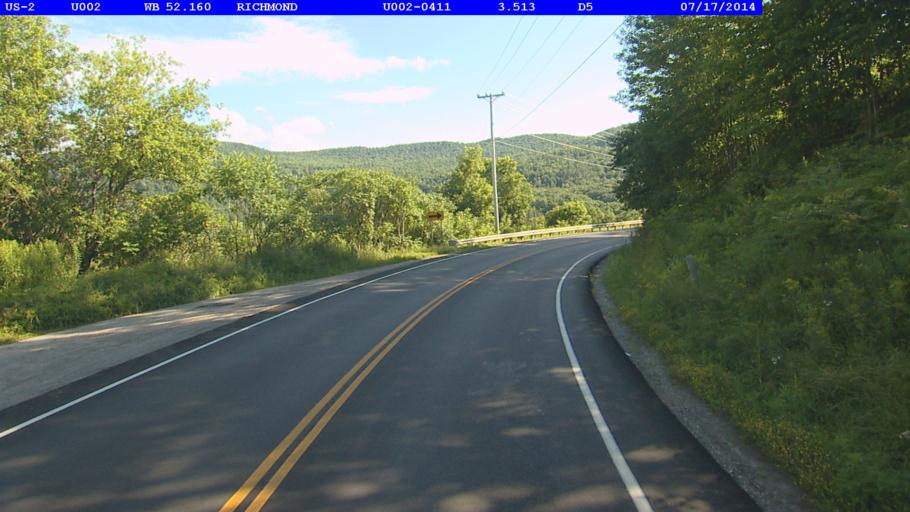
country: US
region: Vermont
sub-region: Chittenden County
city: Williston
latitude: 44.4021
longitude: -72.9795
